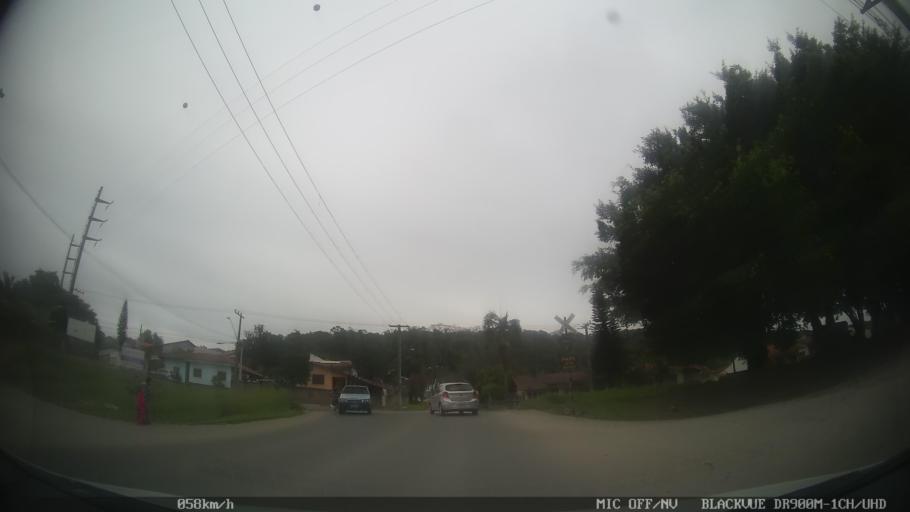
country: BR
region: Santa Catarina
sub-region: Joinville
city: Joinville
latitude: -26.3508
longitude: -48.7964
